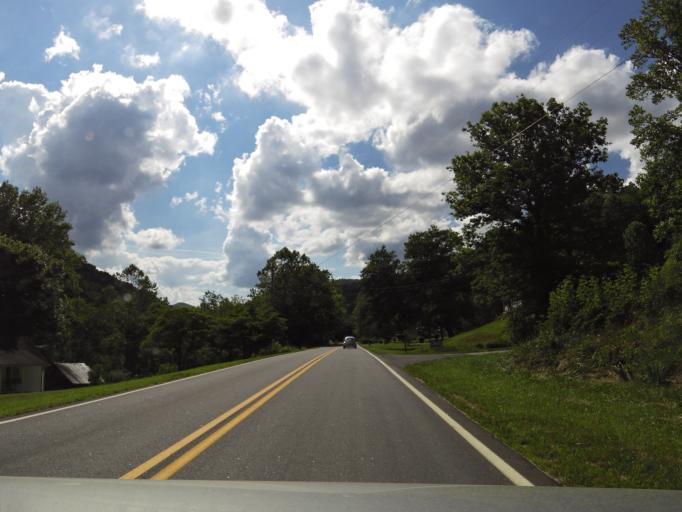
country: US
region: Georgia
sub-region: Towns County
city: Hiawassee
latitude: 34.8332
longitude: -83.7334
